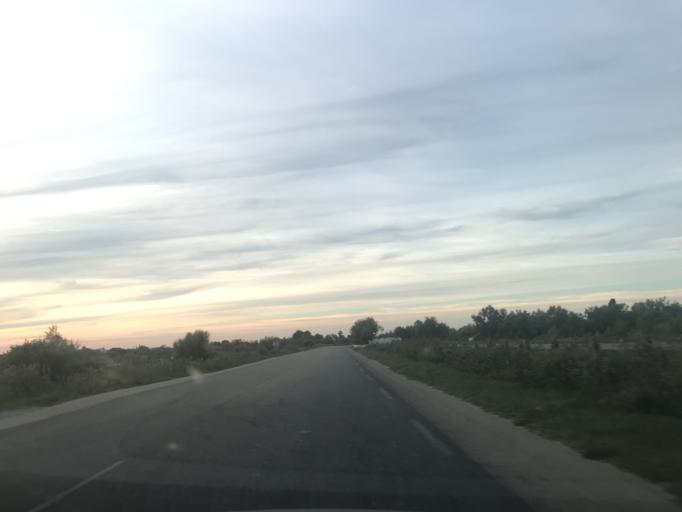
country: FR
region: Provence-Alpes-Cote d'Azur
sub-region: Departement des Bouches-du-Rhone
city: Saintes-Maries-de-la-Mer
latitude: 43.4621
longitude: 4.4209
